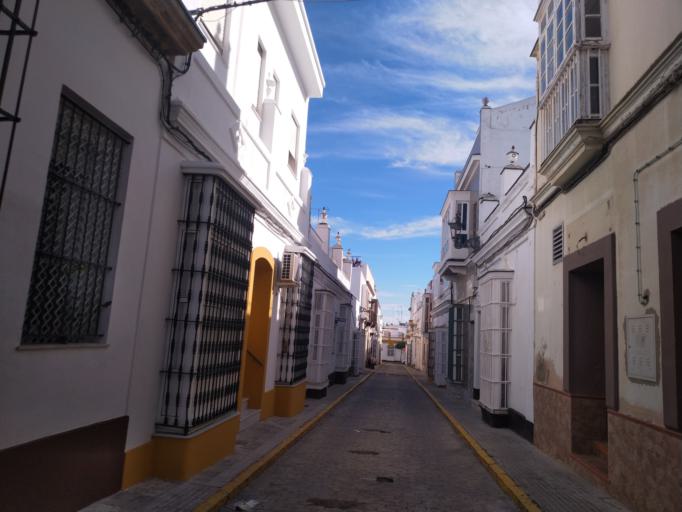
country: ES
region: Andalusia
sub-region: Provincia de Cadiz
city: San Fernando
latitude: 36.4692
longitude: -6.1958
